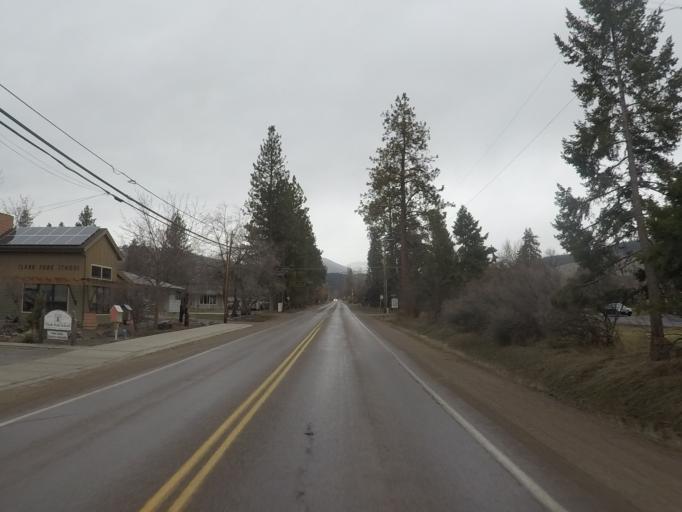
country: US
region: Montana
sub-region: Missoula County
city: East Missoula
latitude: 46.8881
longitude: -113.9657
